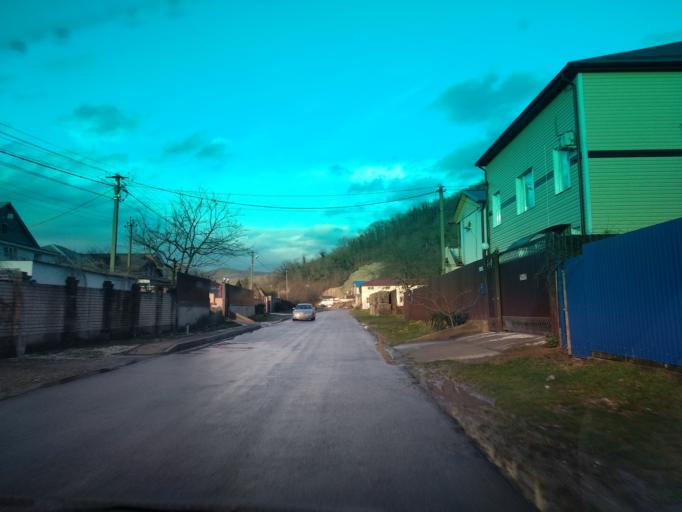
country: RU
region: Krasnodarskiy
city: Novomikhaylovskiy
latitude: 44.2661
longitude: 38.8269
